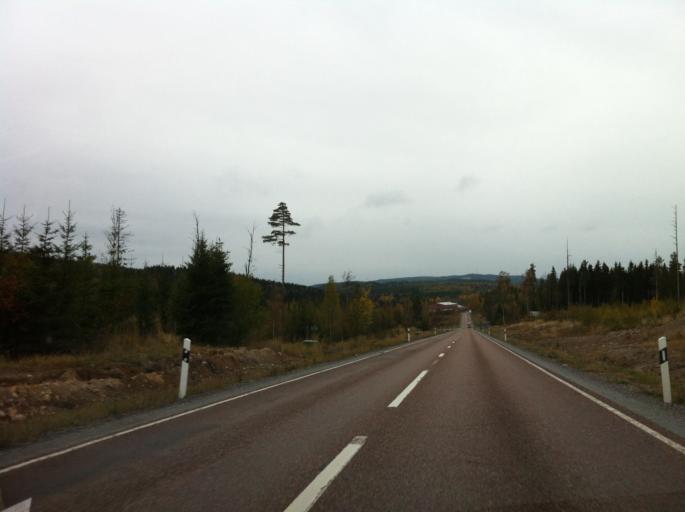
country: SE
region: Dalarna
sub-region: Ludvika Kommun
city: Grangesberg
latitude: 60.0211
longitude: 14.9821
